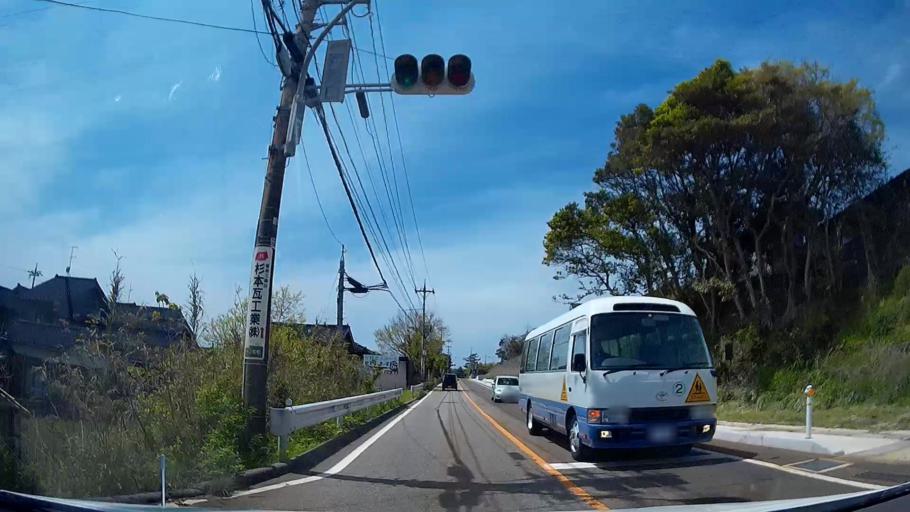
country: JP
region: Ishikawa
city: Hakui
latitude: 36.9241
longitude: 136.7649
